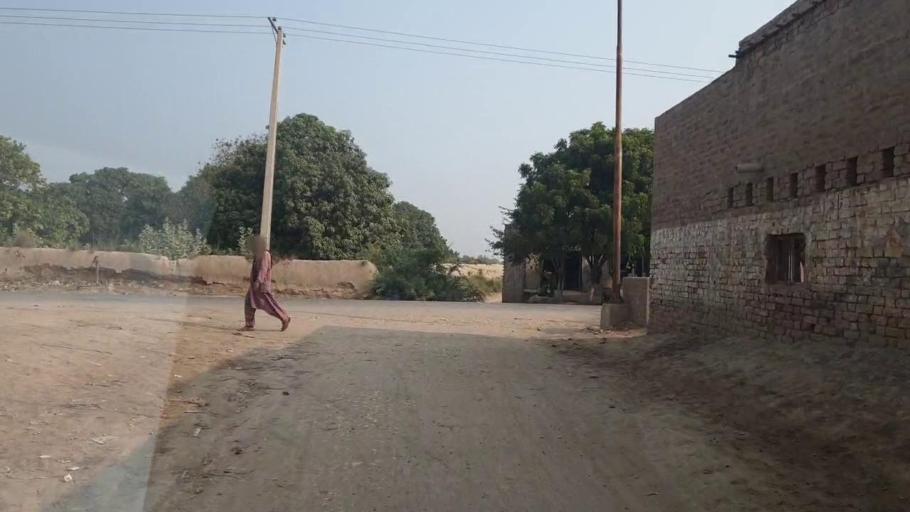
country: PK
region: Sindh
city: Tando Jam
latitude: 25.3395
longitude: 68.5239
